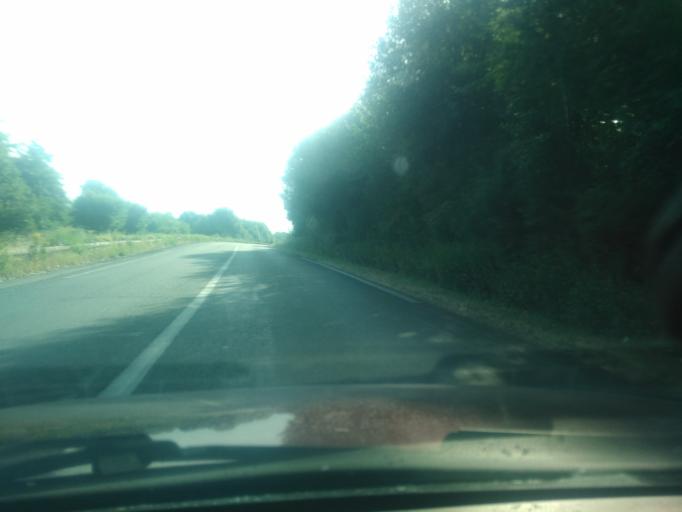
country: FR
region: Pays de la Loire
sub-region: Departement de la Vendee
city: La Chataigneraie
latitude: 46.6565
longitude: -0.7667
